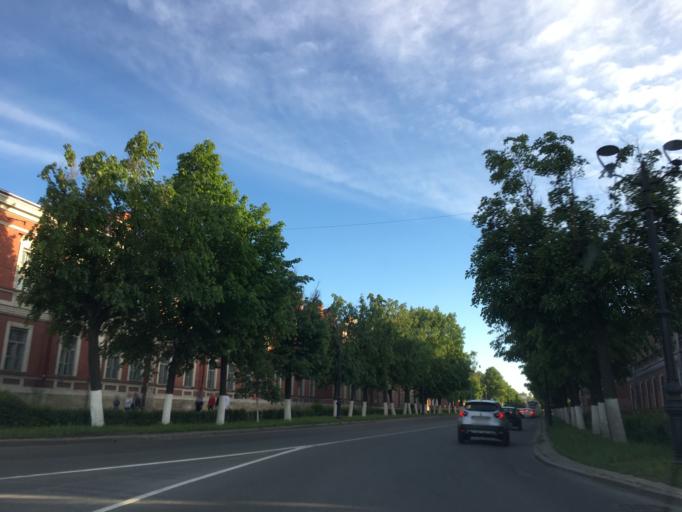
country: RU
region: Leningrad
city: Gatchina
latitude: 59.5764
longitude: 30.1316
